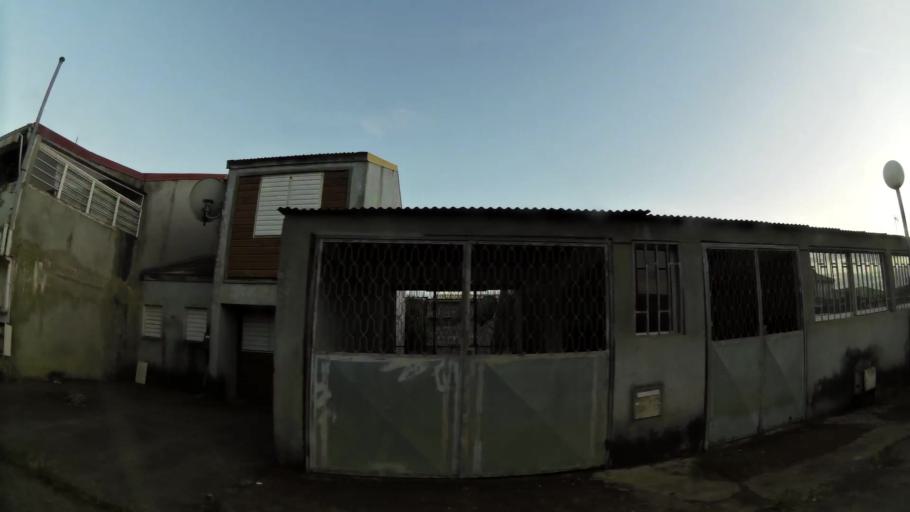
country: GP
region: Guadeloupe
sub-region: Guadeloupe
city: Les Abymes
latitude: 16.2819
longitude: -61.5011
